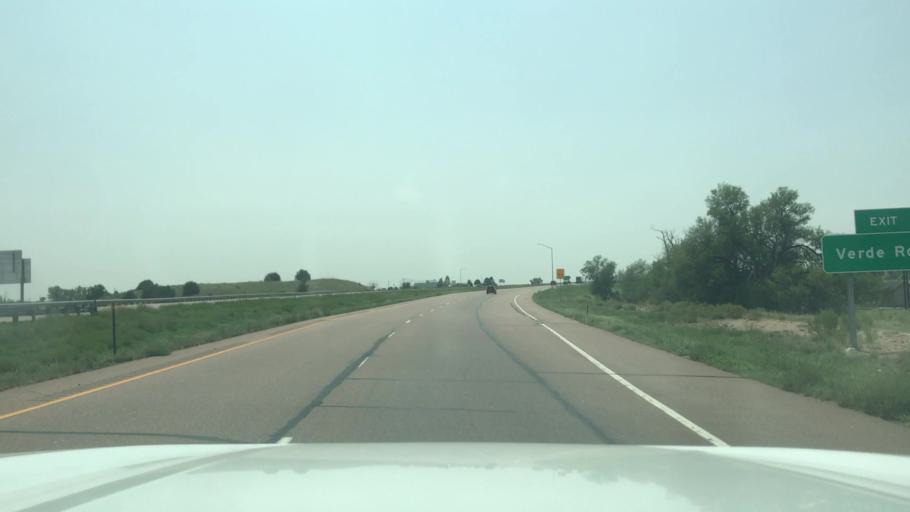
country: US
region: Colorado
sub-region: Pueblo County
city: Pueblo
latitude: 38.1194
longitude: -104.6716
